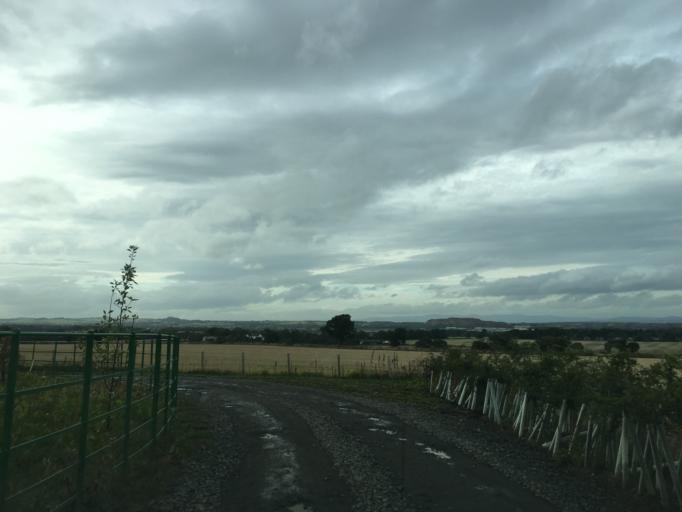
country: GB
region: Scotland
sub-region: West Lothian
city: Kirknewton
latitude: 55.9081
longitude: -3.4192
